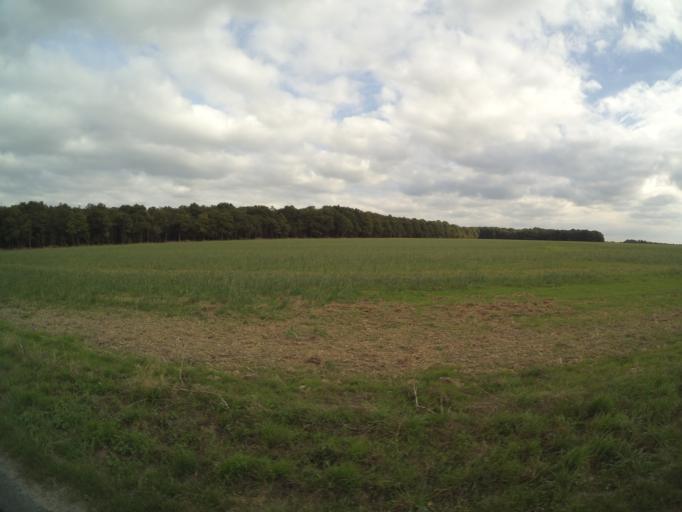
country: FR
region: Centre
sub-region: Departement d'Indre-et-Loire
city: Nazelles-Negron
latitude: 47.4647
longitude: 0.9381
